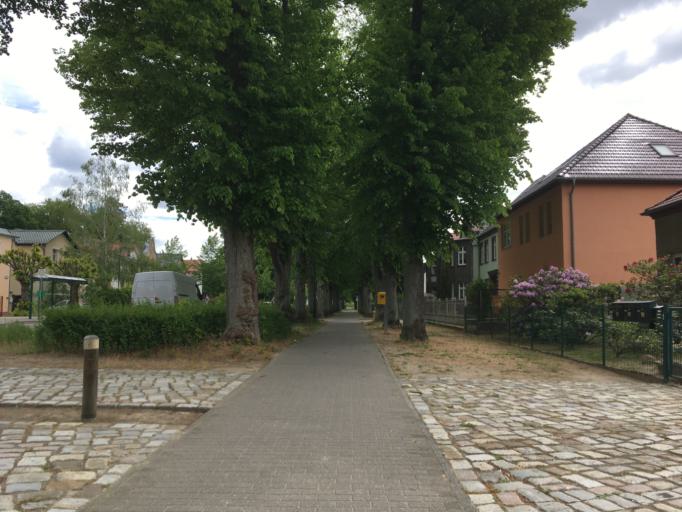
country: DE
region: Brandenburg
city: Biesenthal
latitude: 52.7562
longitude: 13.6697
